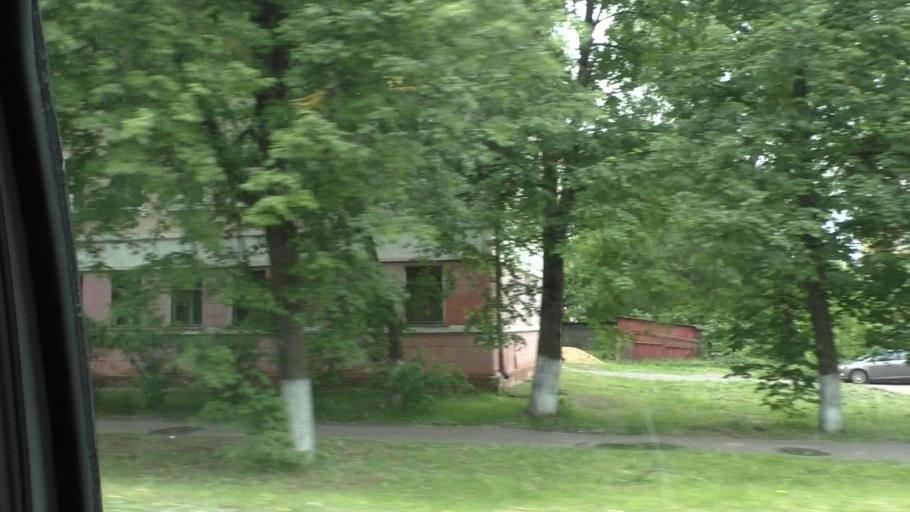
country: RU
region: Moskovskaya
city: Yegor'yevsk
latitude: 55.3923
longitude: 39.0220
